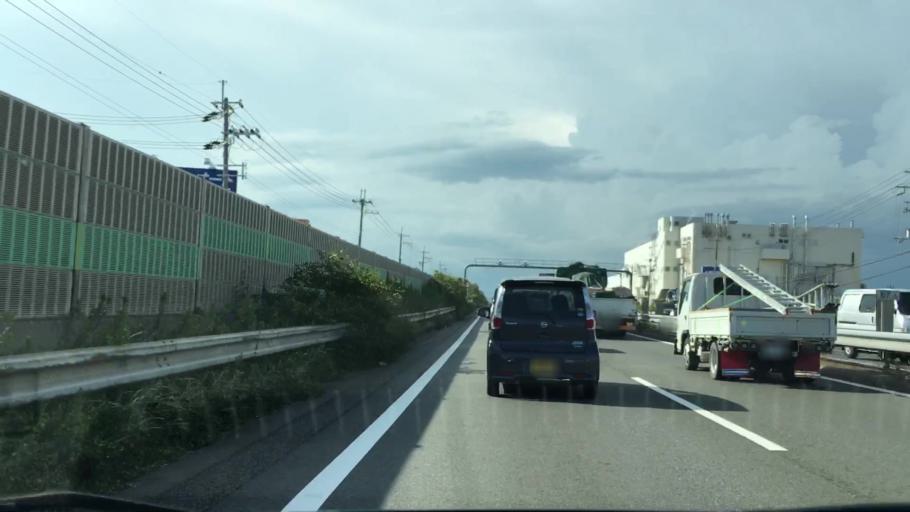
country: JP
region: Hyogo
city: Kakogawacho-honmachi
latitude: 34.7328
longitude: 134.8856
